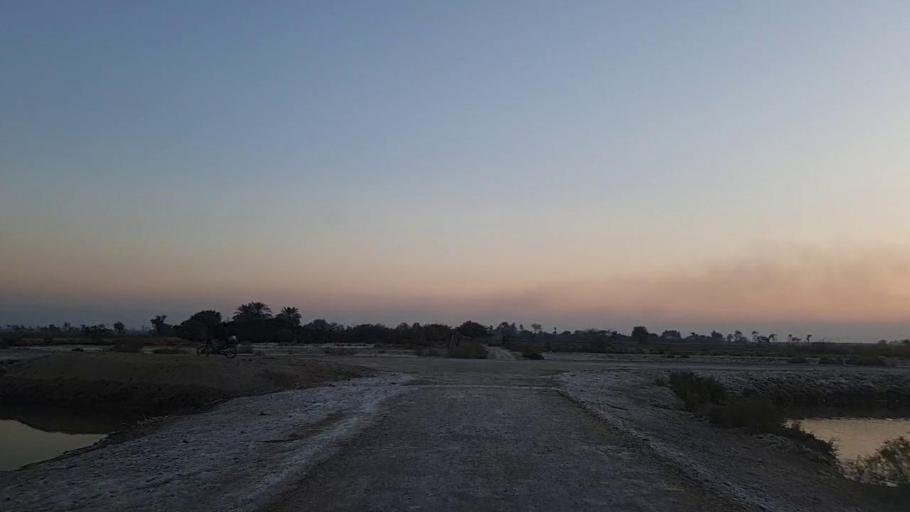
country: PK
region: Sindh
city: Bandhi
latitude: 26.5888
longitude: 68.3359
